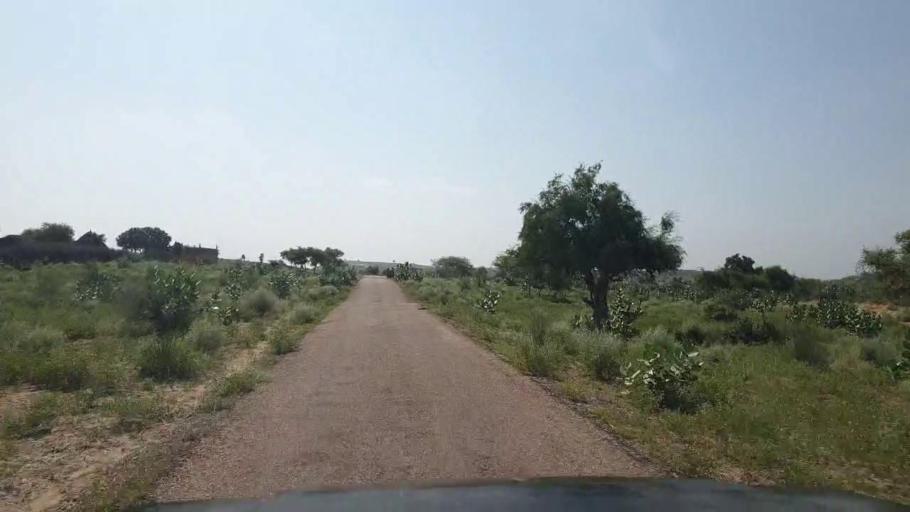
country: PK
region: Sindh
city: Islamkot
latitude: 25.1714
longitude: 70.3989
